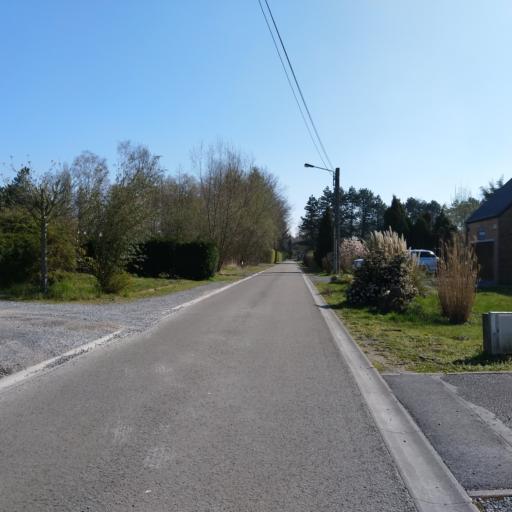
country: BE
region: Wallonia
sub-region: Province du Hainaut
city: Jurbise
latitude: 50.5075
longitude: 3.9325
